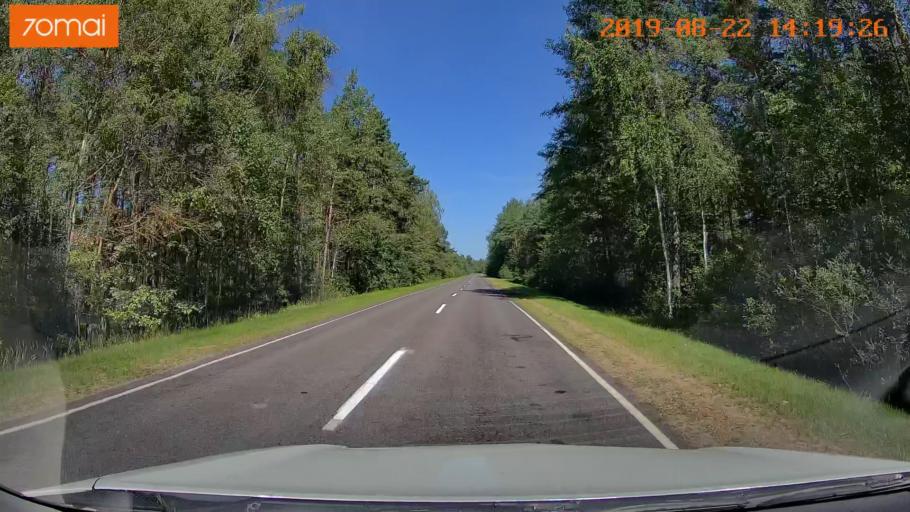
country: BY
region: Mogilev
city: Asipovichy
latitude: 53.2590
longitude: 28.5038
